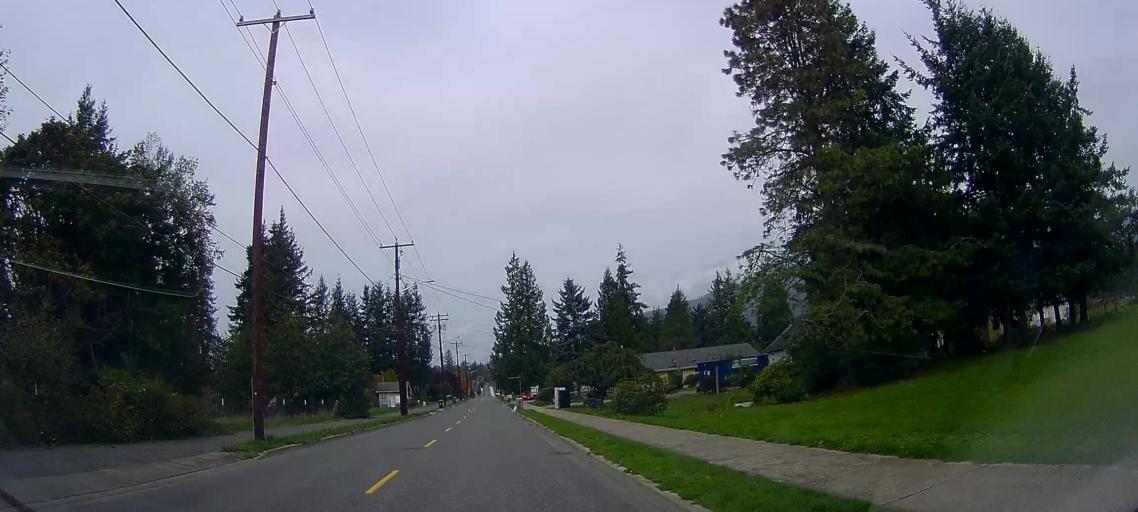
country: US
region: Washington
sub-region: Skagit County
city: Sedro-Woolley
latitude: 48.5191
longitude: -122.2105
